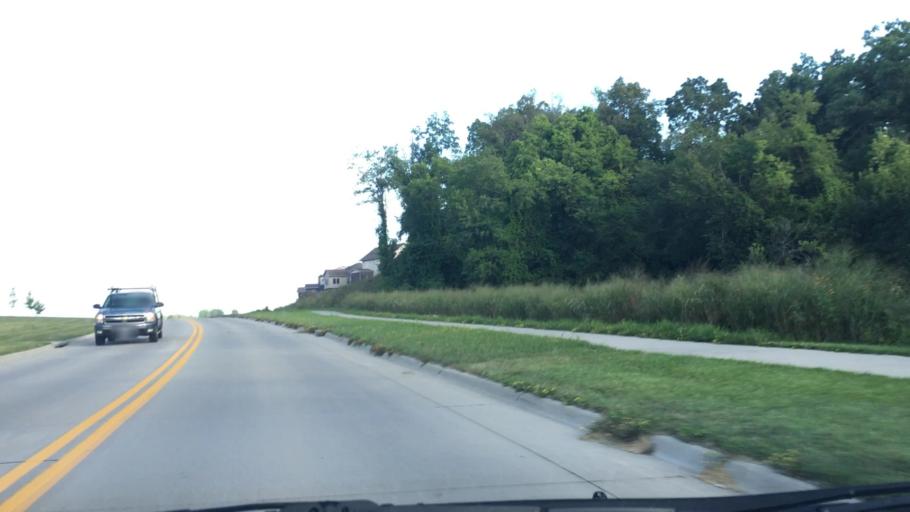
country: US
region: Iowa
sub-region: Johnson County
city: Coralville
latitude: 41.7008
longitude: -91.5518
